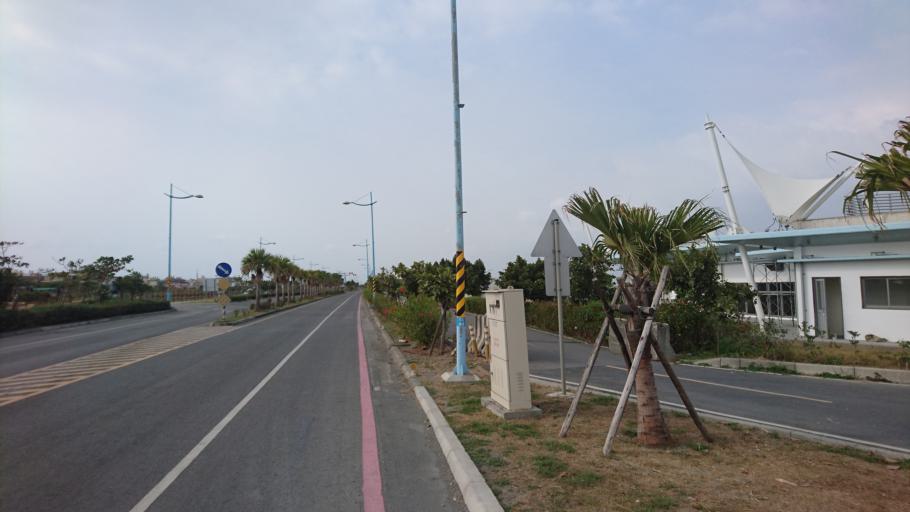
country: TW
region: Taiwan
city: Fengshan
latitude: 22.4379
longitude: 120.4743
